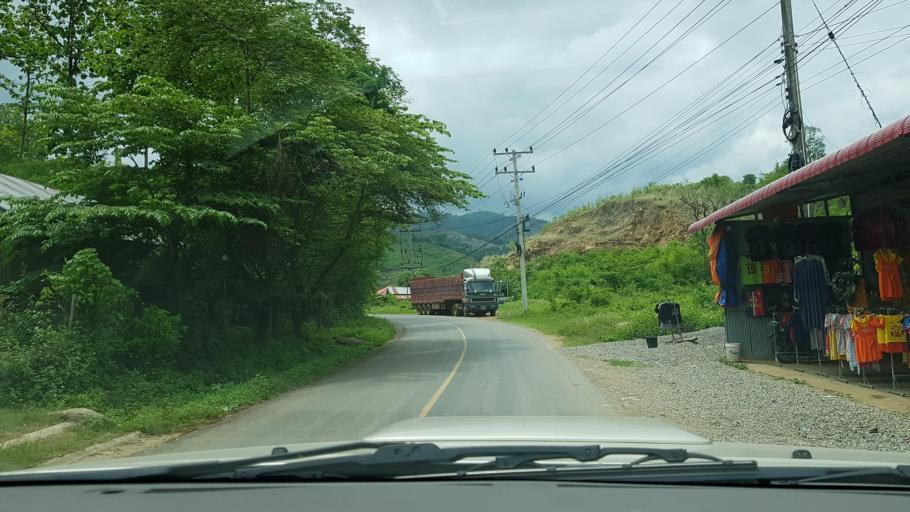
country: TH
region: Nan
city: Chaloem Phra Kiat
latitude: 19.9700
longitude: 101.2678
